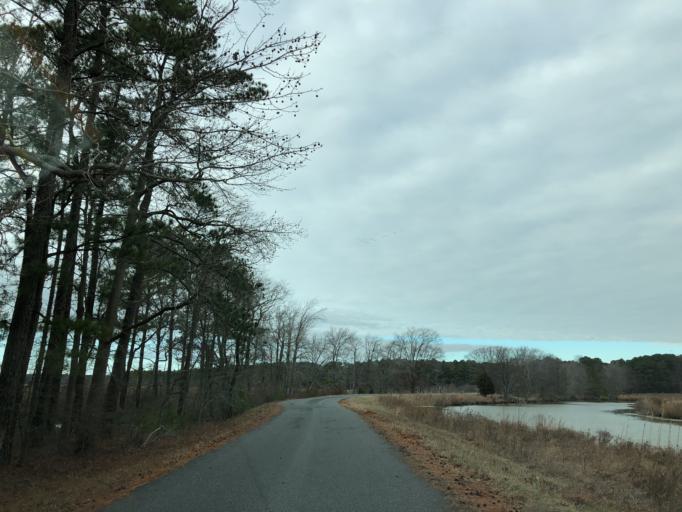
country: US
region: Maryland
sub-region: Dorchester County
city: Cambridge
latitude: 38.4425
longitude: -76.1231
